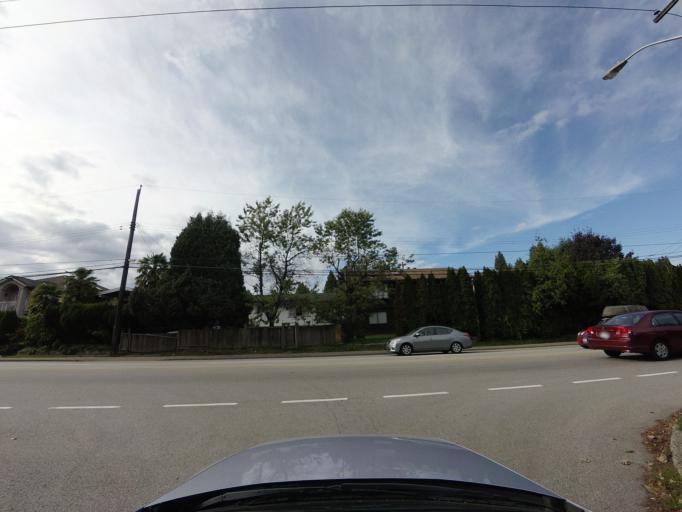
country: CA
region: British Columbia
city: New Westminster
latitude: 49.2200
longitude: -122.9256
